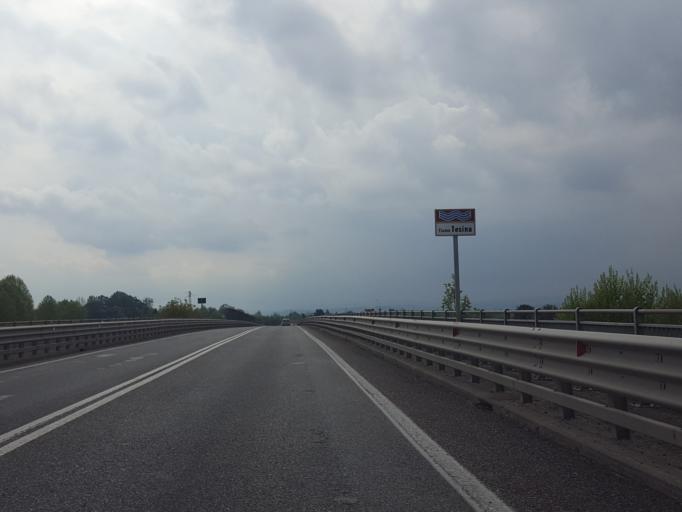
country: IT
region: Veneto
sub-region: Provincia di Vicenza
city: Lisiera
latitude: 45.5832
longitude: 11.6172
